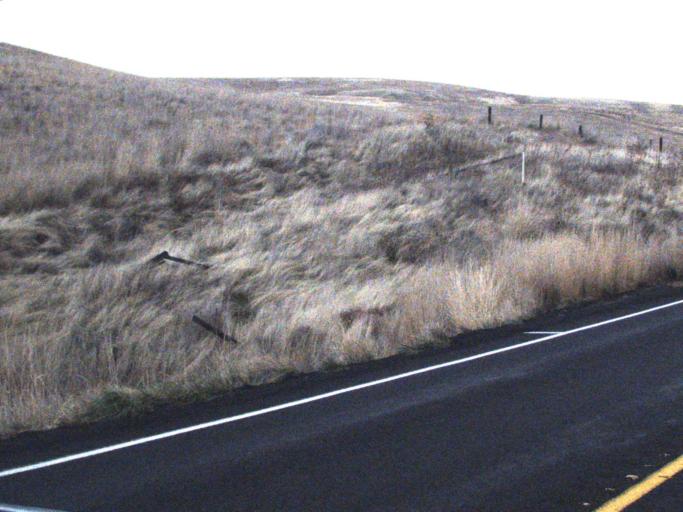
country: US
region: Washington
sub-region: Columbia County
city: Dayton
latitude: 46.4655
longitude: -117.9615
